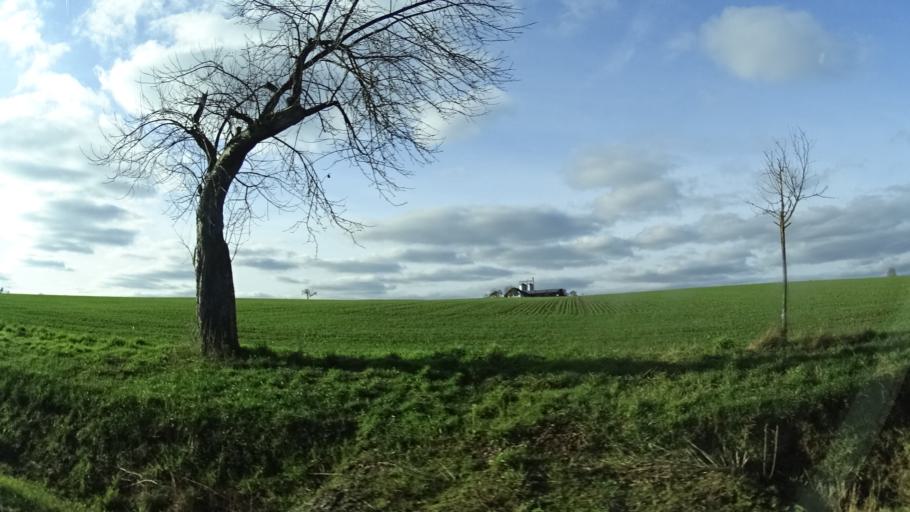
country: DE
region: Bavaria
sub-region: Regierungsbezirk Unterfranken
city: Rollbach
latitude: 49.7504
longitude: 9.2421
